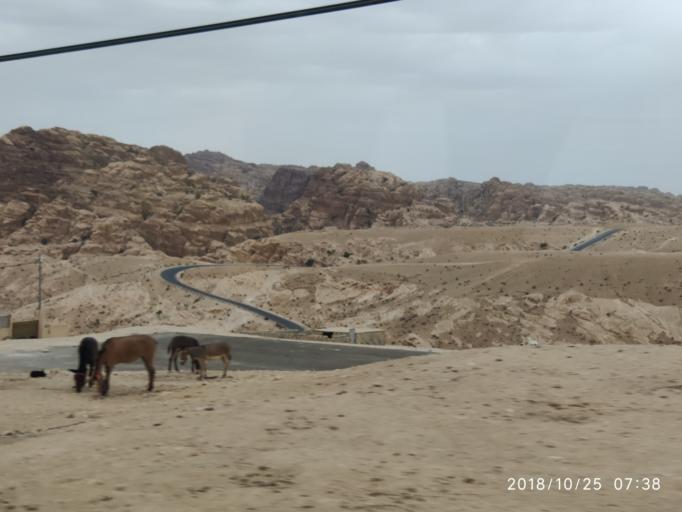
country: JO
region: Ma'an
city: Petra
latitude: 30.3444
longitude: 35.4595
